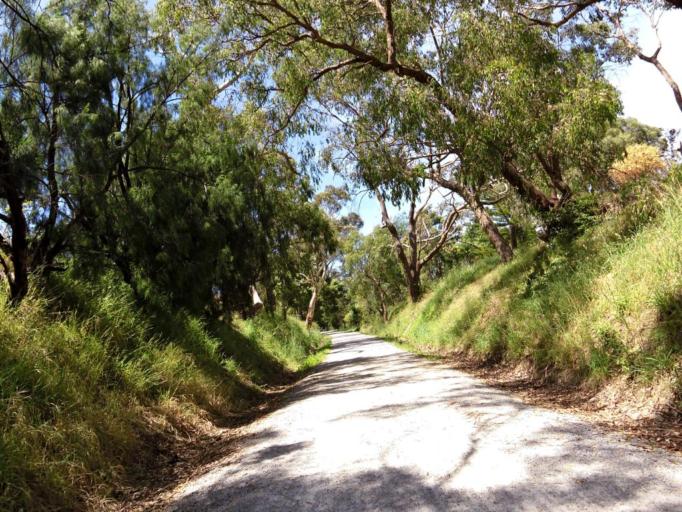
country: AU
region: Victoria
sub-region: Yarra Ranges
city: Lilydale
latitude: -37.7596
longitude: 145.3610
